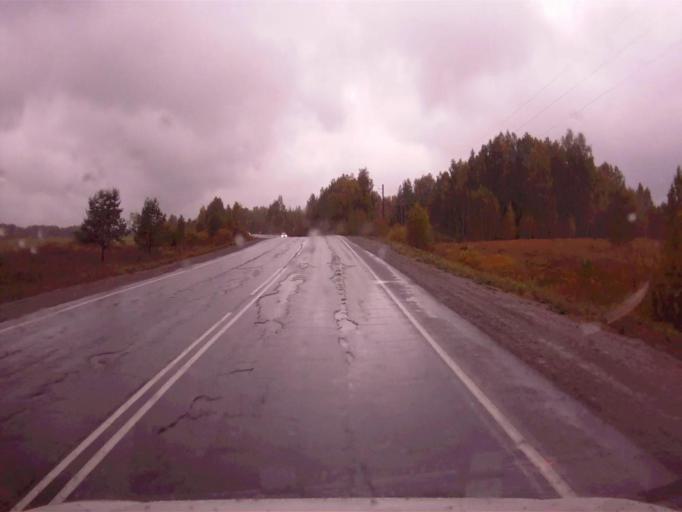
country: RU
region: Chelyabinsk
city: Argayash
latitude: 55.4856
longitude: 60.7392
